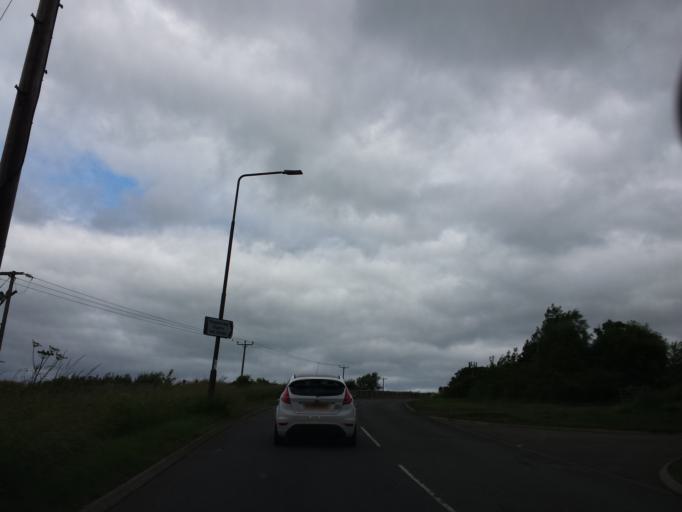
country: GB
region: Scotland
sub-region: East Lothian
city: Haddington
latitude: 55.9611
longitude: -2.7907
